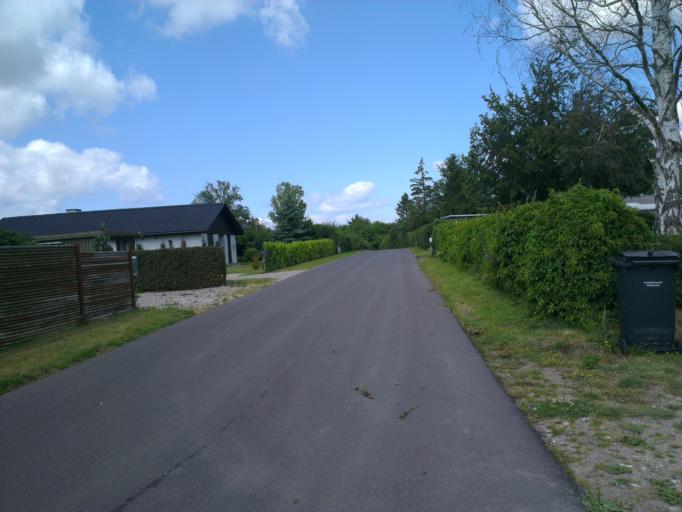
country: DK
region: Zealand
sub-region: Lejre Kommune
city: Ejby
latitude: 55.7452
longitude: 11.8746
